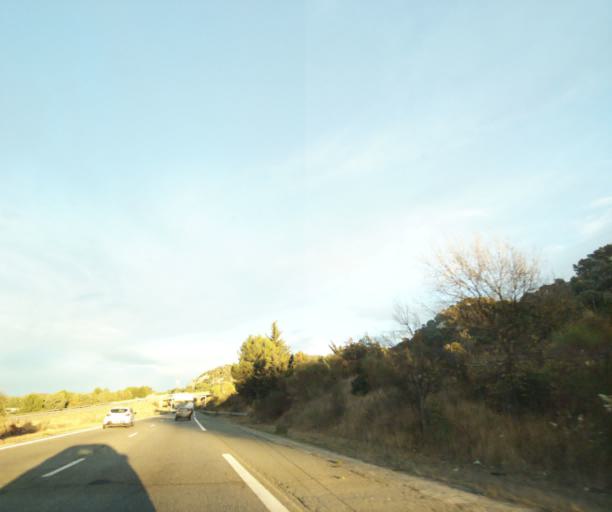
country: FR
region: Provence-Alpes-Cote d'Azur
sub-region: Departement des Bouches-du-Rhone
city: Les Pennes-Mirabeau
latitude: 43.3987
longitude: 5.2915
